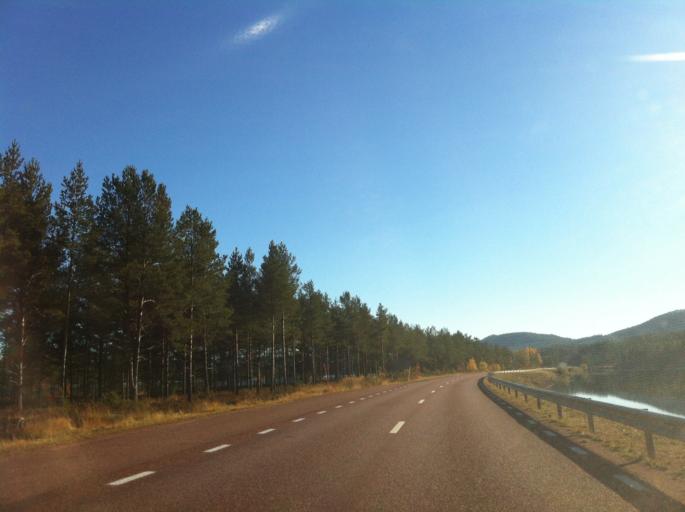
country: SE
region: Dalarna
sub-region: Alvdalens Kommun
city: AElvdalen
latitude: 61.3120
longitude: 13.6819
